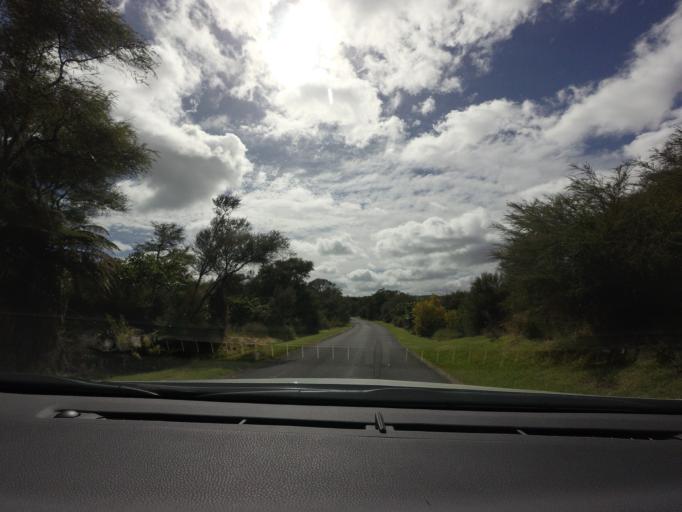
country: NZ
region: Bay of Plenty
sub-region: Rotorua District
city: Rotorua
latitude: -38.3496
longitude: 176.3722
